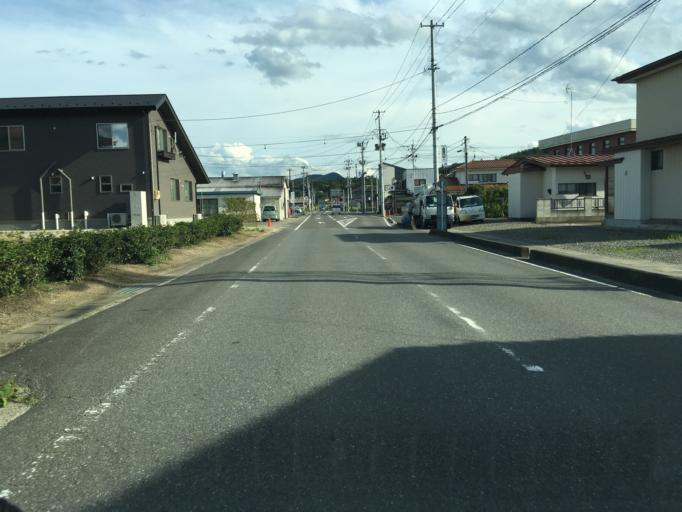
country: JP
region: Fukushima
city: Hobaramachi
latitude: 37.8136
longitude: 140.5411
